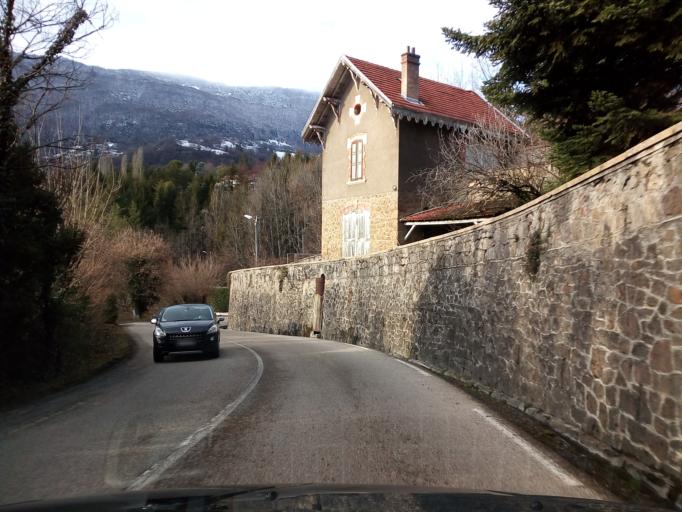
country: FR
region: Rhone-Alpes
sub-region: Departement de l'Isere
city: Corenc
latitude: 45.2180
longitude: 5.7599
